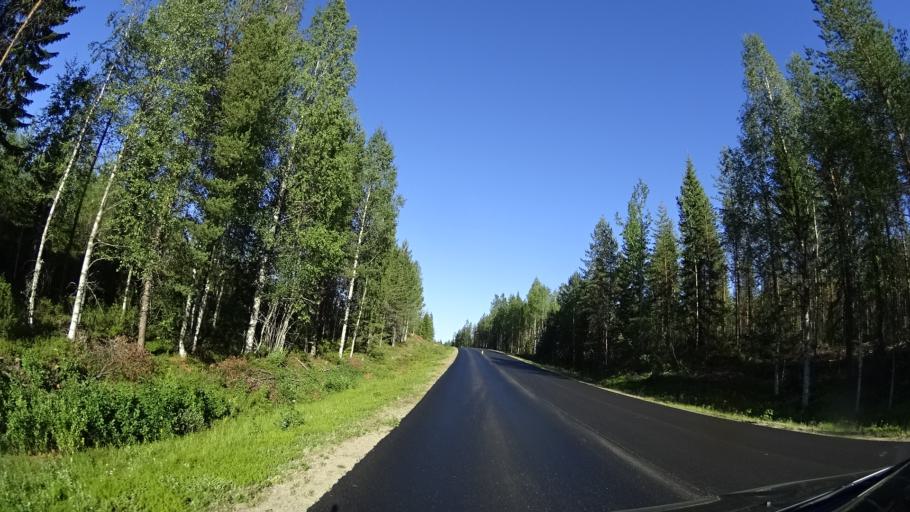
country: FI
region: North Karelia
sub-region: Pielisen Karjala
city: Valtimo
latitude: 63.5608
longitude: 28.5955
